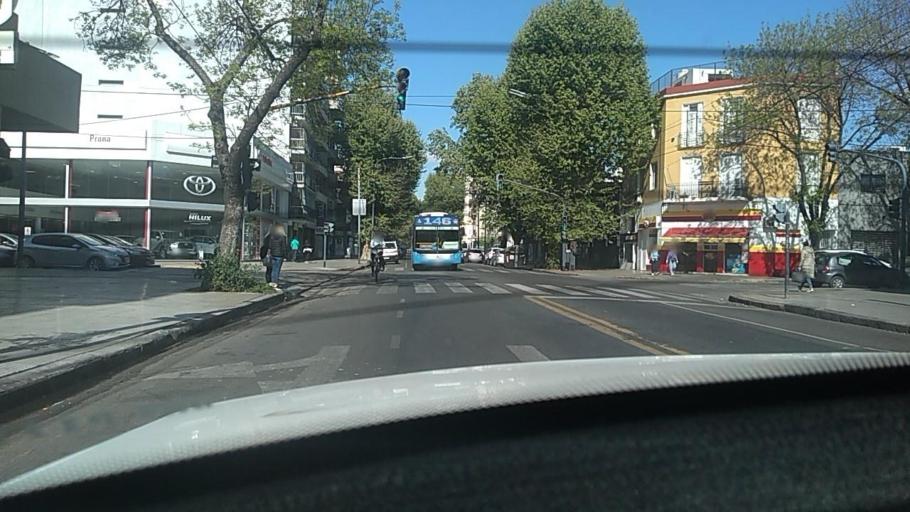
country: AR
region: Buenos Aires F.D.
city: Villa Santa Rita
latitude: -34.5997
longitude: -58.5019
